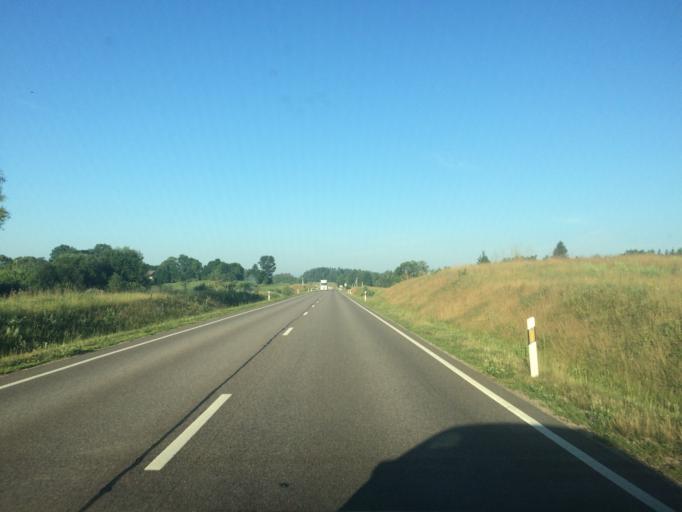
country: LT
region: Utenos apskritis
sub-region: Anyksciai
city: Anyksciai
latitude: 55.4146
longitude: 25.2078
